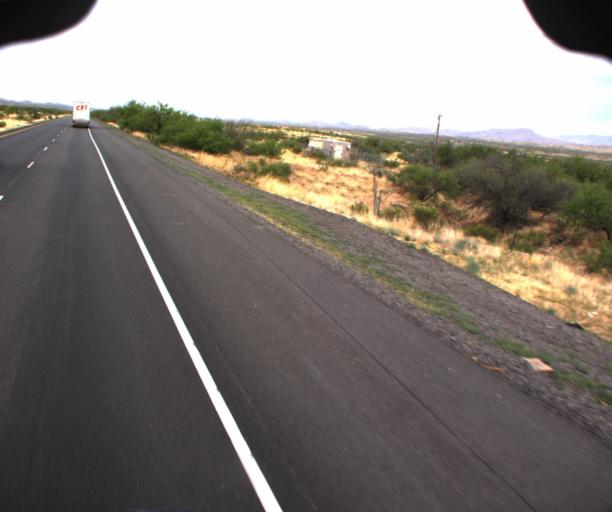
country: US
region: Arizona
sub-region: Cochise County
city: Mescal
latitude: 31.9735
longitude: -110.4915
